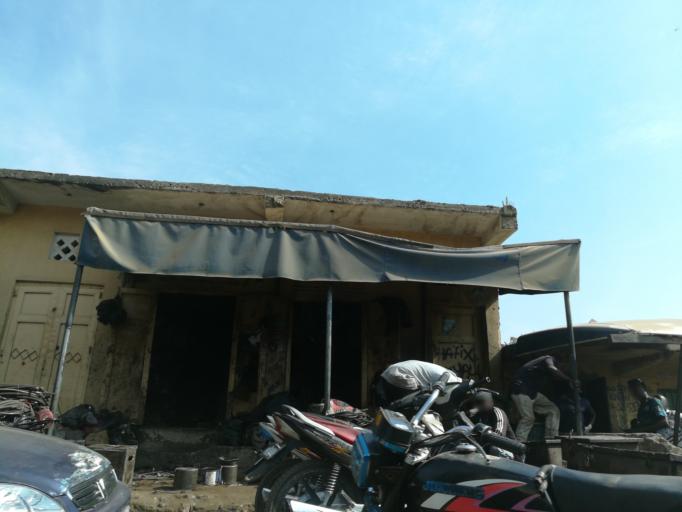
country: NG
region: Kano
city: Kano
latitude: 12.0145
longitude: 8.5244
